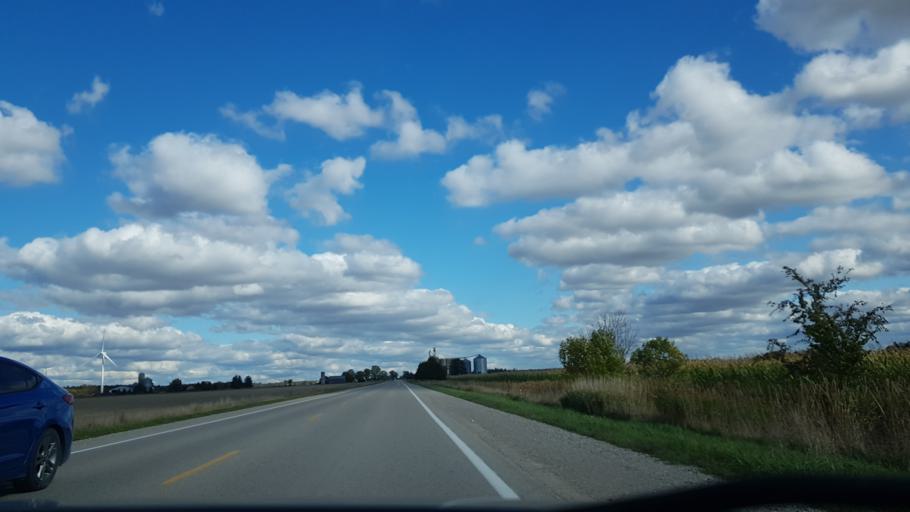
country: CA
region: Ontario
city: Lambton Shores
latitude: 43.2387
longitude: -81.7537
